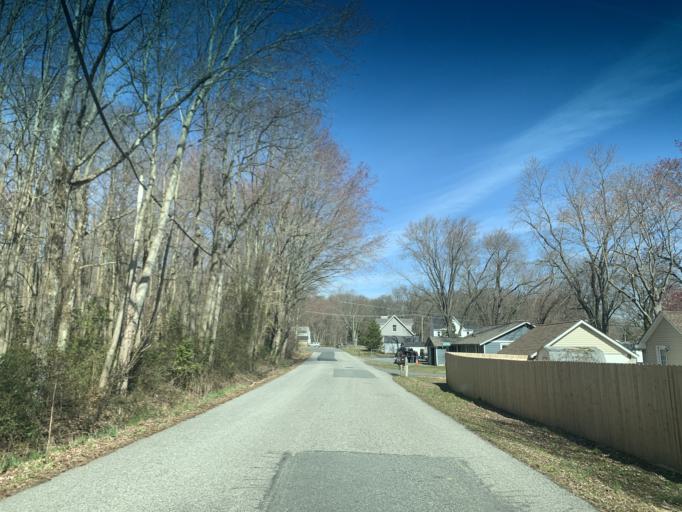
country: US
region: Maryland
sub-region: Cecil County
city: Charlestown
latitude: 39.5462
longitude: -76.0084
